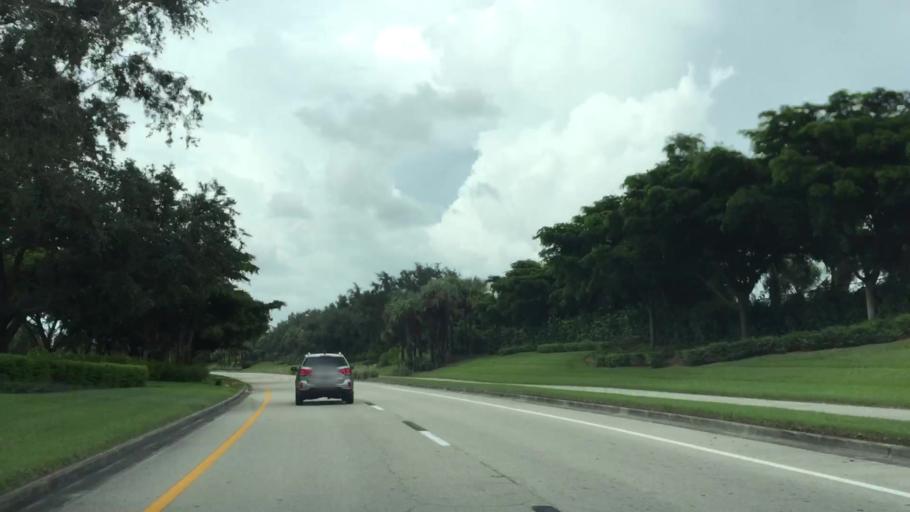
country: US
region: Florida
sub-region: Lee County
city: Estero
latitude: 26.4056
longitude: -81.7821
